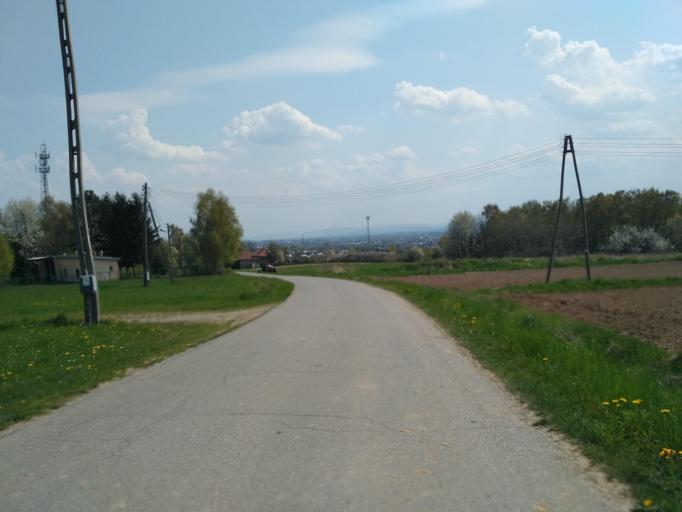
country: PL
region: Subcarpathian Voivodeship
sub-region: Powiat krosnienski
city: Jedlicze
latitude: 49.7321
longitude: 21.6388
